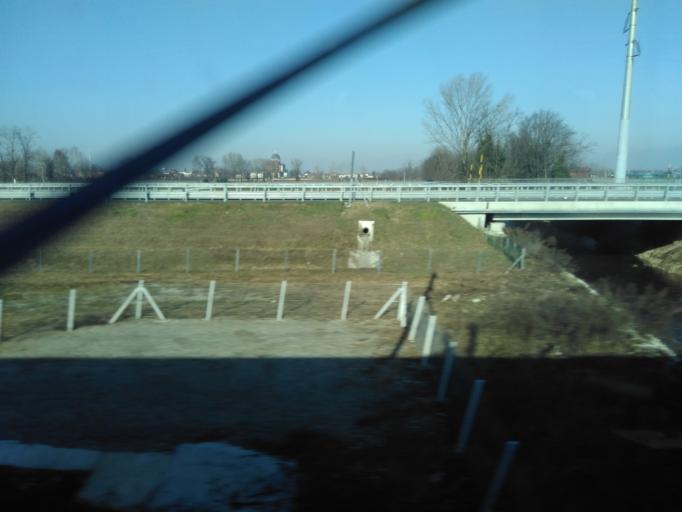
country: IT
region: Lombardy
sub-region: Provincia di Bergamo
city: Calcio
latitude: 45.4961
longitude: 9.8548
